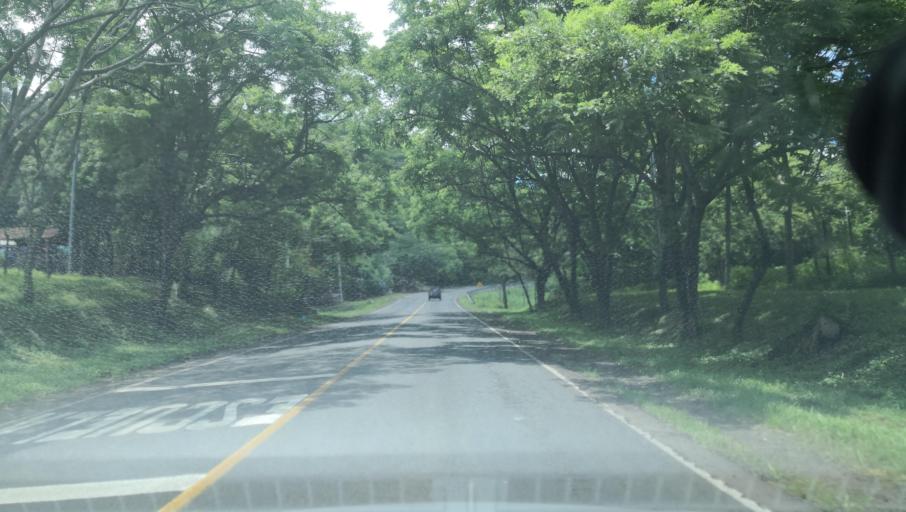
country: NI
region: Esteli
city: Condega
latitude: 13.3032
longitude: -86.3502
